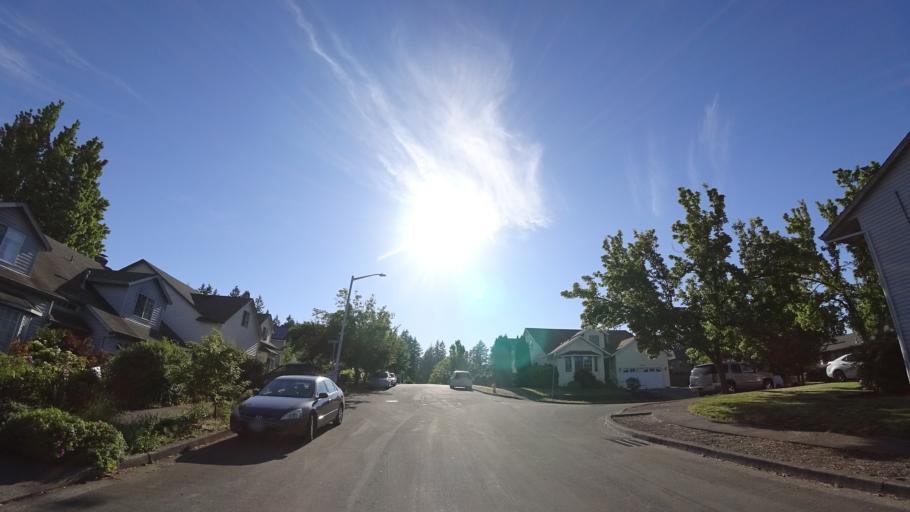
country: US
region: Oregon
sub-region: Washington County
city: Beaverton
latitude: 45.4635
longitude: -122.8140
